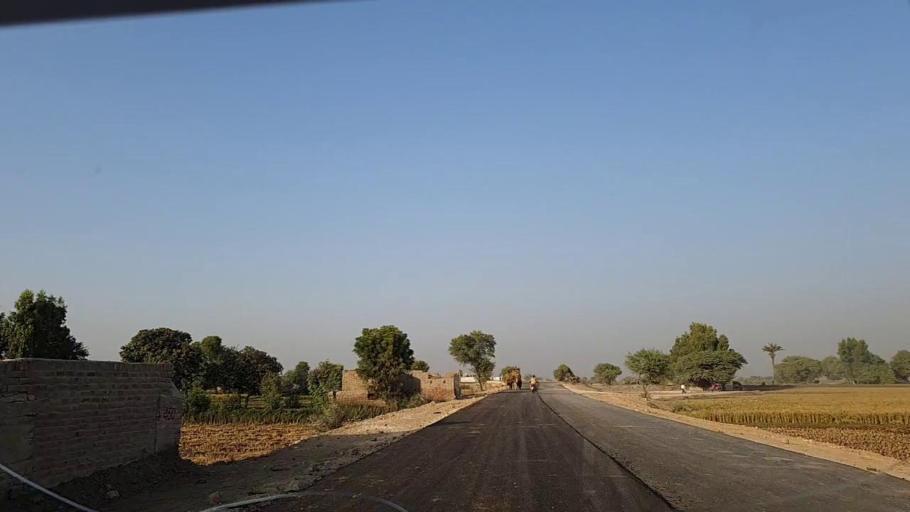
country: PK
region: Sindh
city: Rustam jo Goth
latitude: 27.9722
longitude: 68.8040
